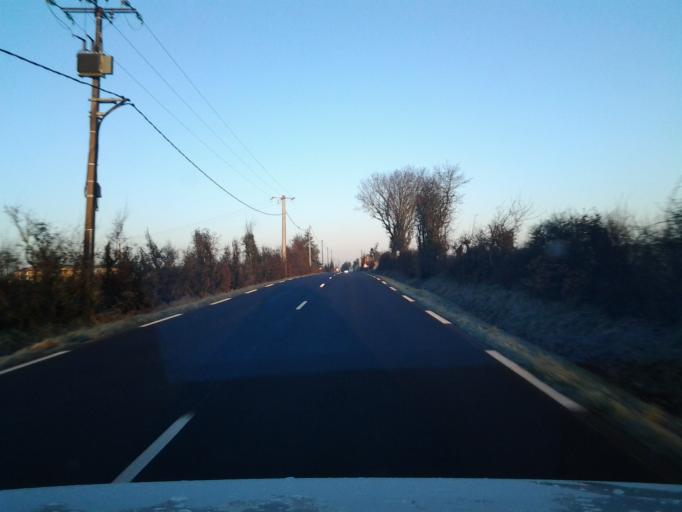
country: FR
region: Pays de la Loire
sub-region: Departement de la Vendee
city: La Gaubretiere
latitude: 46.9528
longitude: -1.0831
